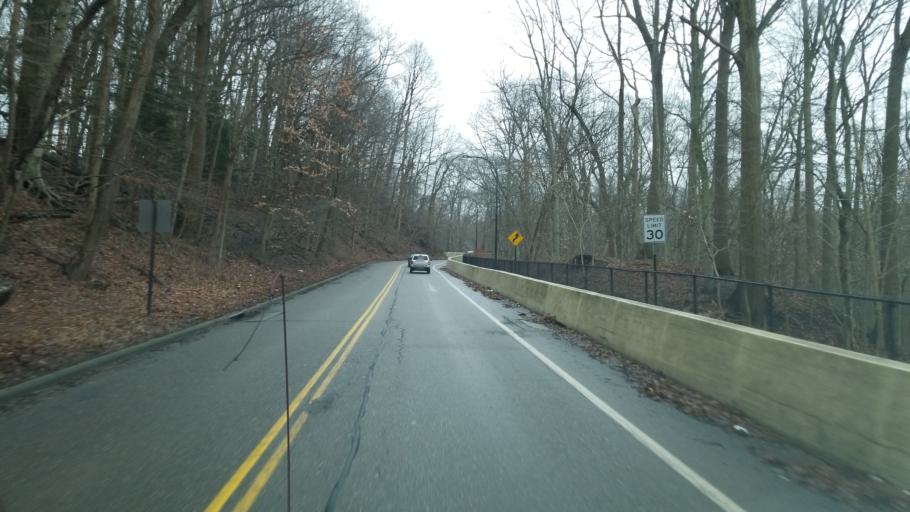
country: US
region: Ohio
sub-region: Summit County
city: Akron
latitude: 41.1285
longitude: -81.5515
